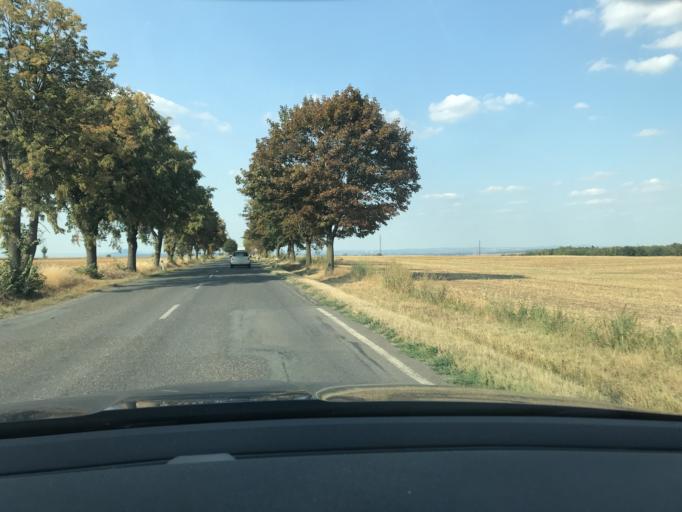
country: CZ
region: Central Bohemia
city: Kralupy nad Vltavou
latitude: 50.2089
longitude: 14.3159
